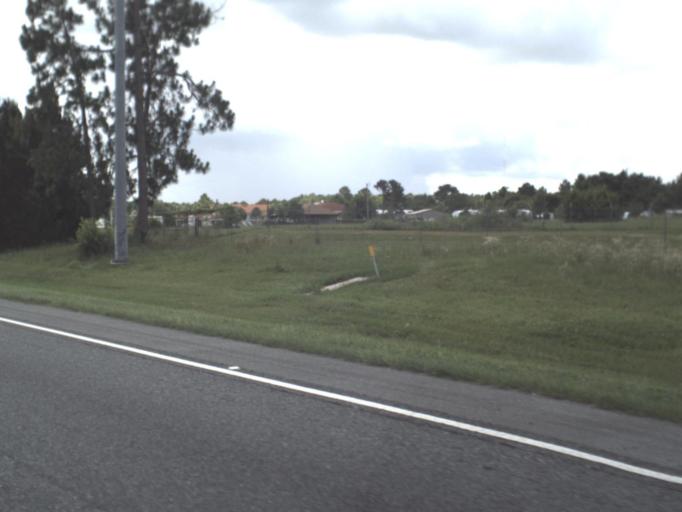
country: US
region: Florida
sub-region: Columbia County
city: Lake City
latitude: 30.1203
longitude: -82.6575
